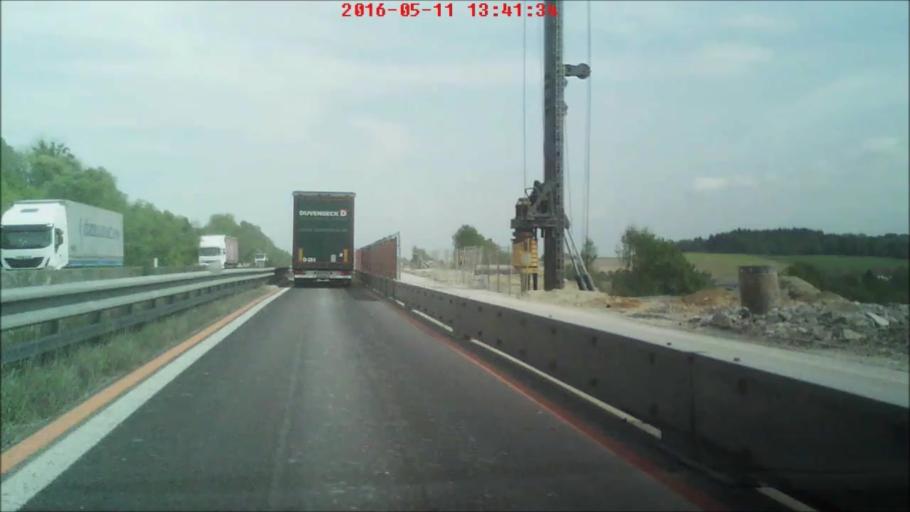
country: AT
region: Upper Austria
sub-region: Politischer Bezirk Ried im Innkreis
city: Ried im Innkreis
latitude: 48.2399
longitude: 13.5640
